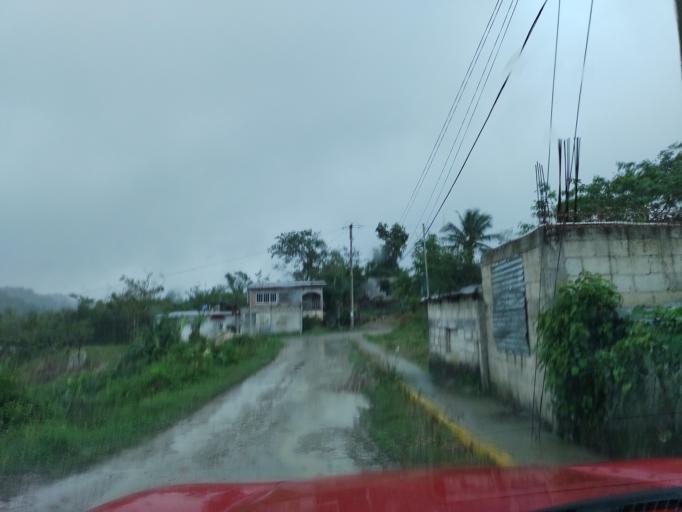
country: MX
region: Veracruz
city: Papantla de Olarte
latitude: 20.4329
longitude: -97.3382
